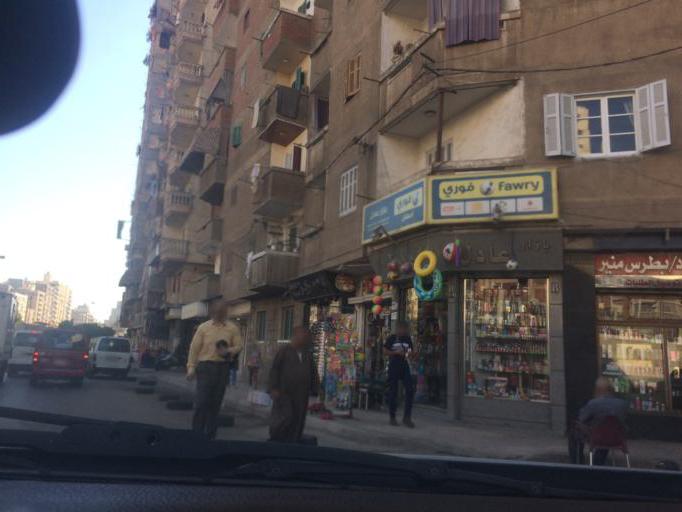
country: EG
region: Alexandria
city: Alexandria
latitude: 31.2588
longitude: 29.9958
